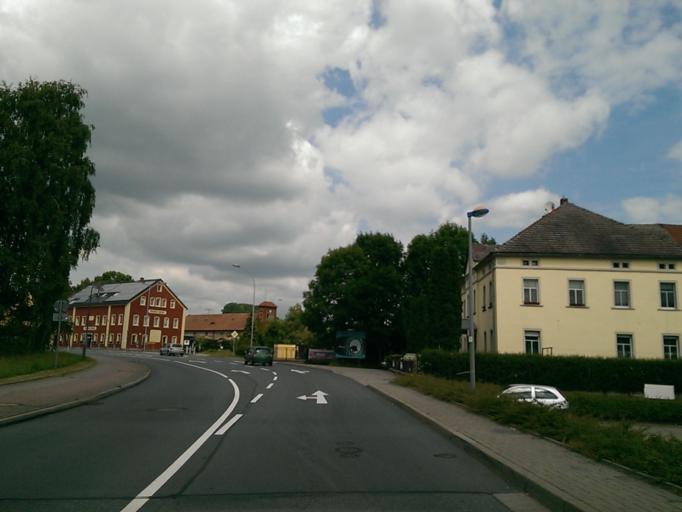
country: DE
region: Saxony
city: Eibau
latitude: 50.9750
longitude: 14.6971
